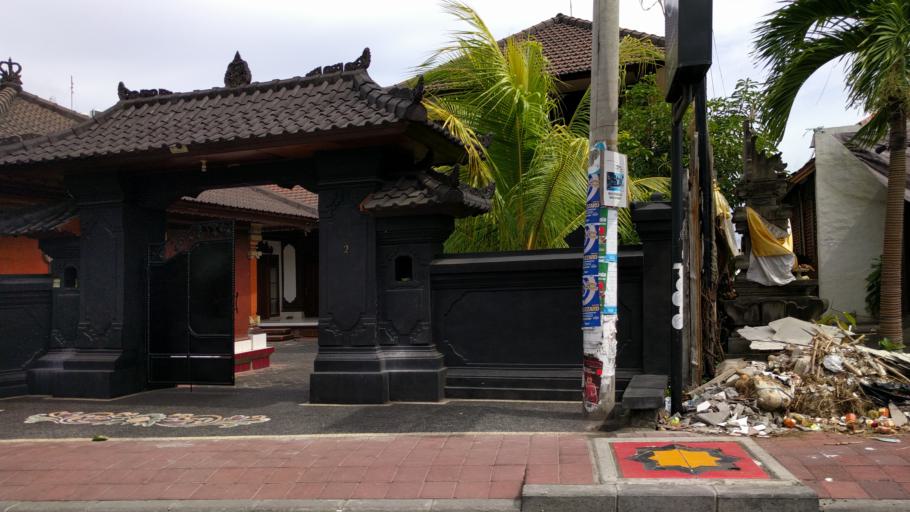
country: ID
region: Bali
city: Kuta
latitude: -8.6716
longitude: 115.1597
